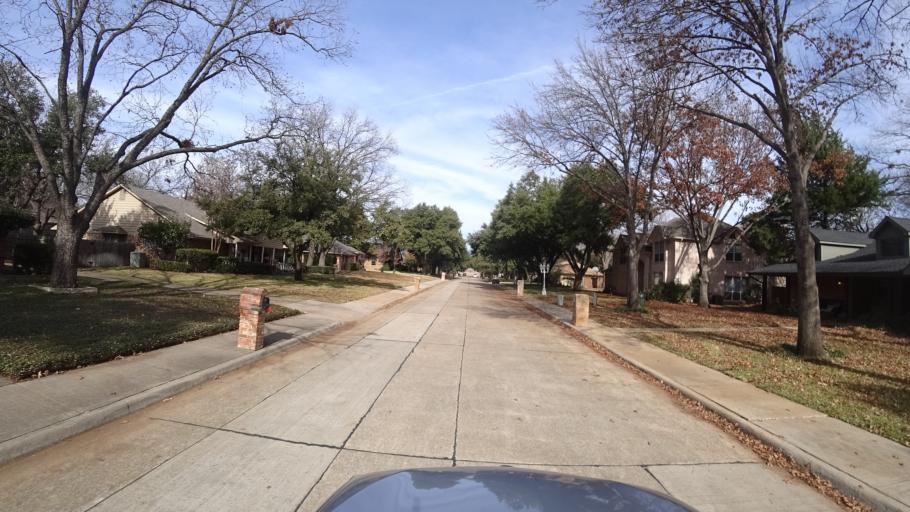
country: US
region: Texas
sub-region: Denton County
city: Highland Village
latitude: 33.0778
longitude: -97.0441
